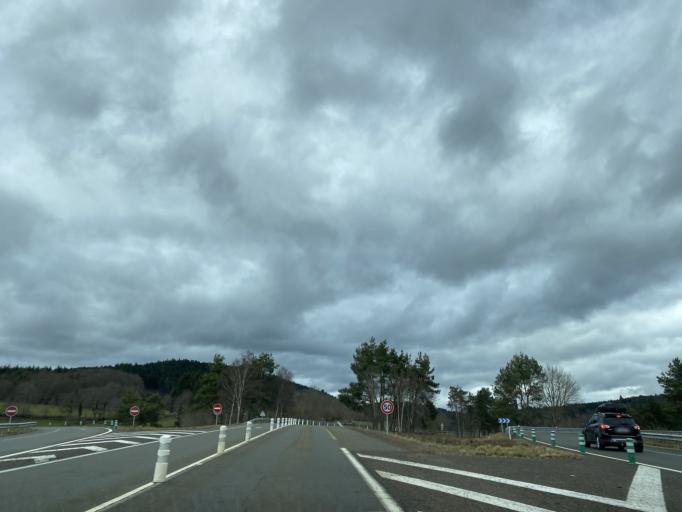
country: FR
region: Rhone-Alpes
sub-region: Departement de la Loire
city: Noiretable
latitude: 45.8523
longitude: 3.7917
